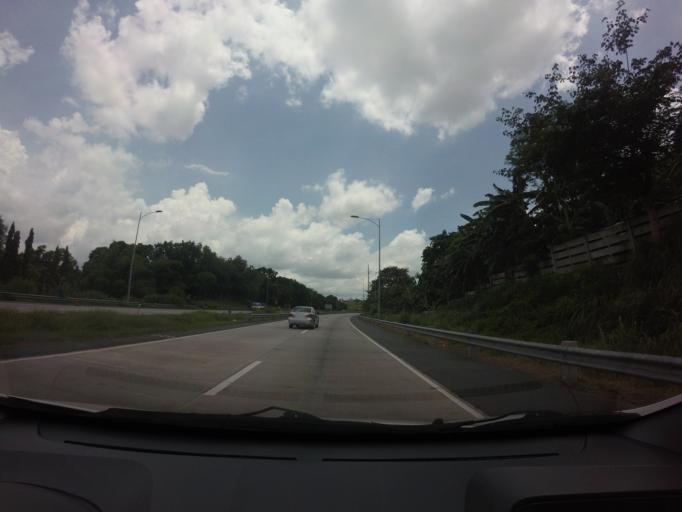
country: PH
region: Calabarzon
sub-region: Province of Laguna
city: San Pedro
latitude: 14.3792
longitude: 121.0317
